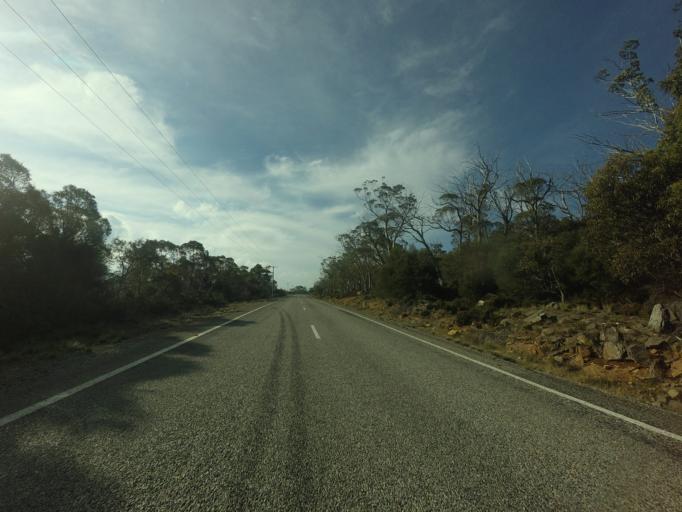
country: AU
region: Tasmania
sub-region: Meander Valley
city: Deloraine
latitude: -41.9887
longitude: 146.7098
